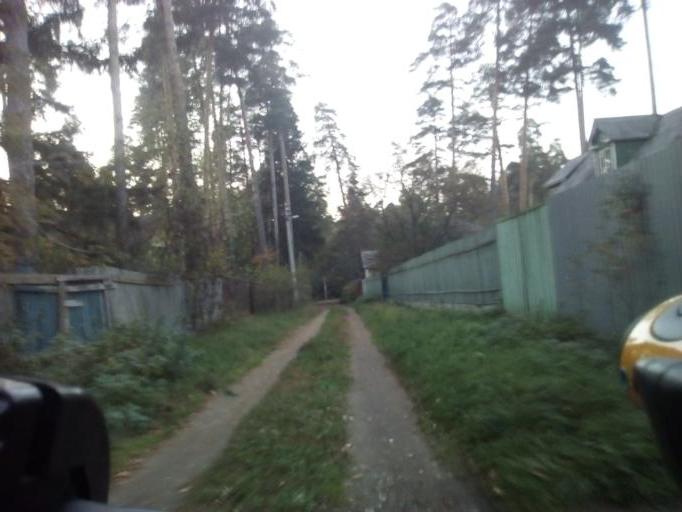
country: RU
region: Moskovskaya
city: Kratovo
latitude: 55.5958
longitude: 38.1863
